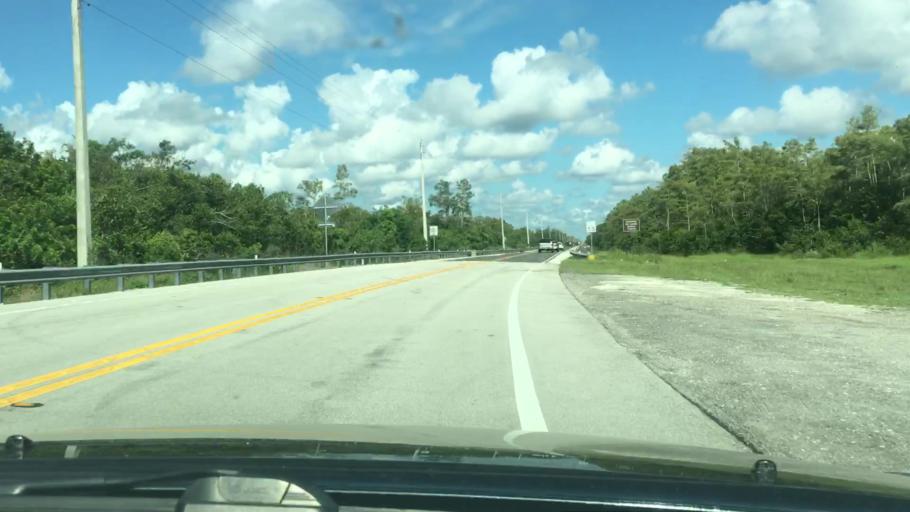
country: US
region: Florida
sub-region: Miami-Dade County
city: Kendall West
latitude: 25.7632
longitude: -80.8296
